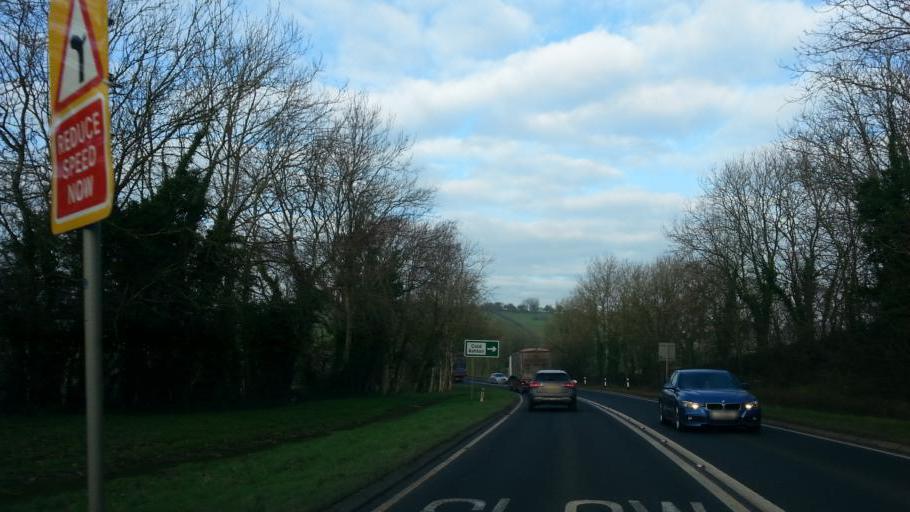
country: GB
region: England
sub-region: South Gloucestershire
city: Cold Ashton
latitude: 51.4437
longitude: -2.3648
